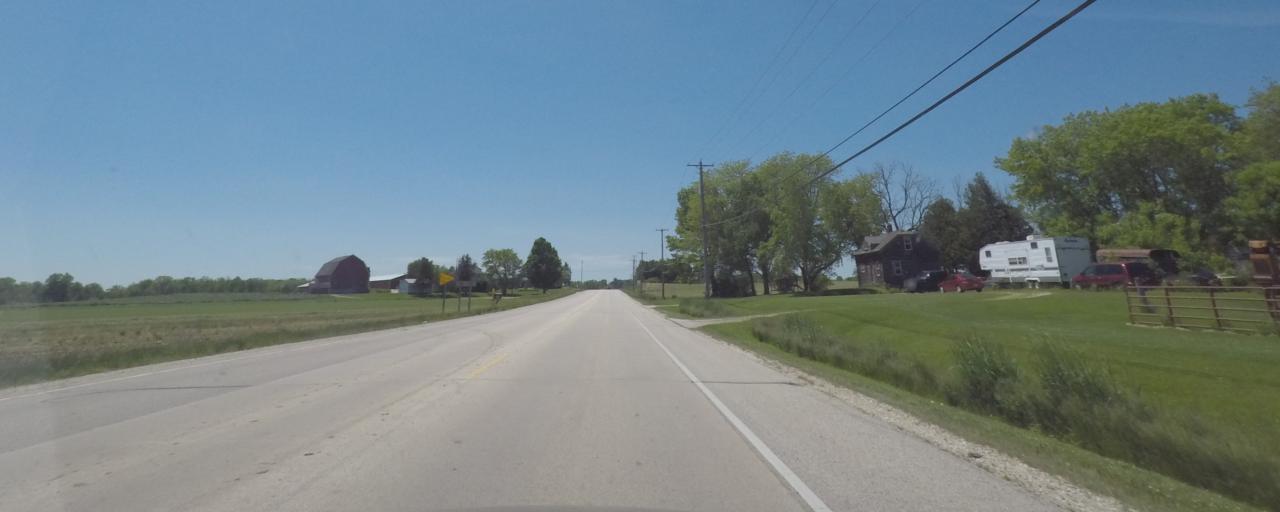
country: US
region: Wisconsin
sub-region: Washington County
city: West Bend
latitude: 43.4684
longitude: -88.1495
